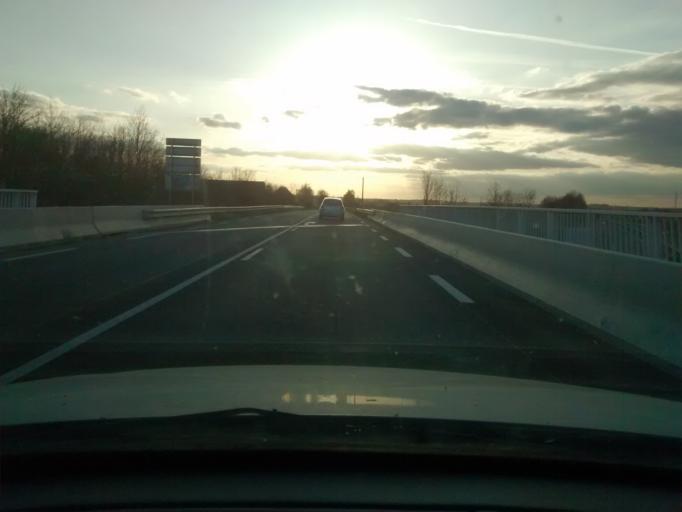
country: FR
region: Pays de la Loire
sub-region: Departement de la Mayenne
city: Sainte-Suzanne
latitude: 48.0333
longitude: -0.3575
